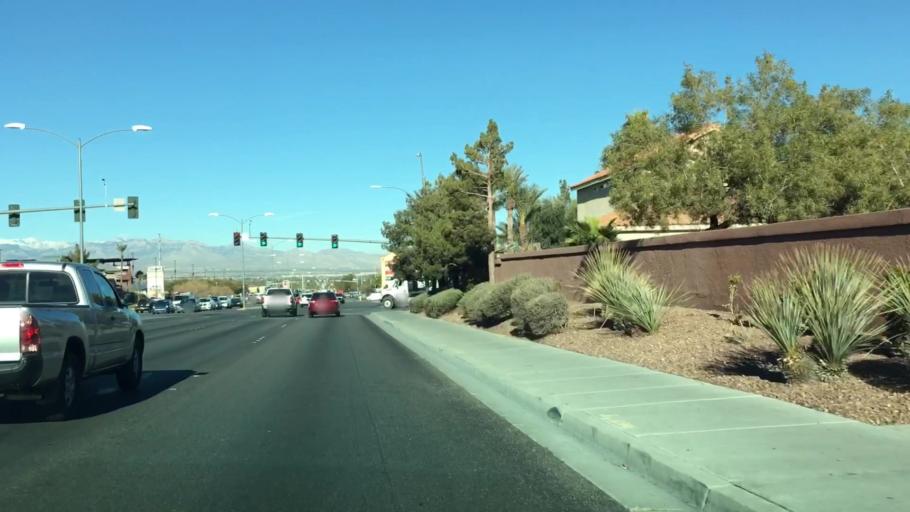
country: US
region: Nevada
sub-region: Clark County
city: Whitney
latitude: 36.0042
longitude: -115.1106
